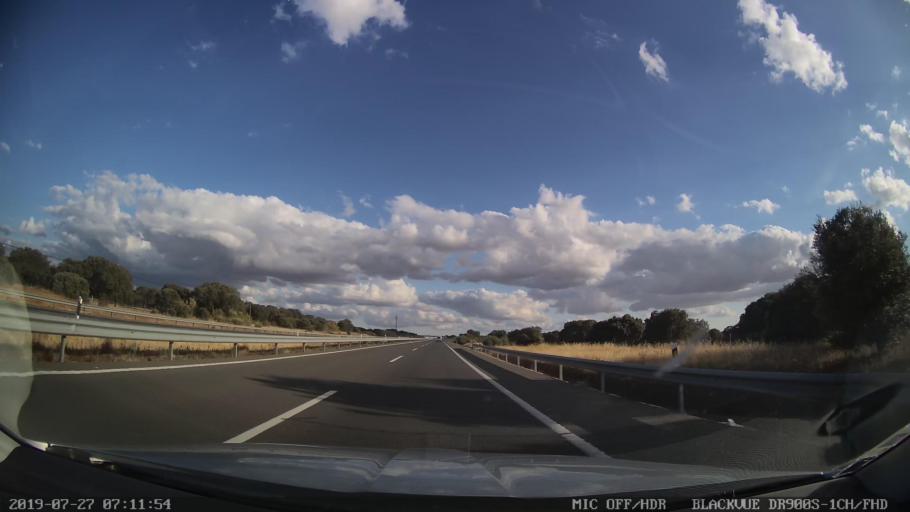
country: ES
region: Extremadura
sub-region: Provincia de Caceres
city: Torrecillas de la Tiesa
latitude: 39.5433
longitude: -5.8335
